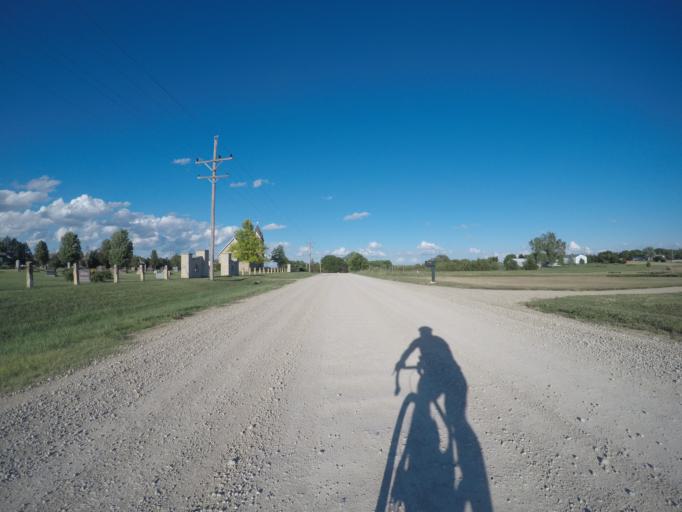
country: US
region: Kansas
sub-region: Riley County
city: Manhattan
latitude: 39.2616
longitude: -96.6843
